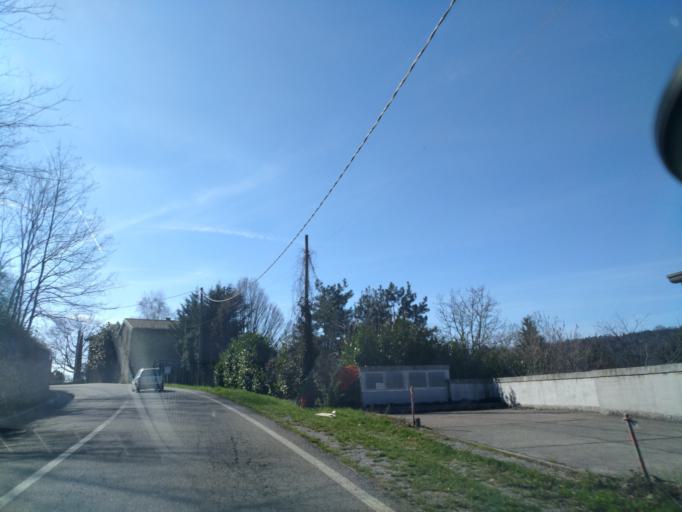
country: IT
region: Lombardy
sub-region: Provincia di Como
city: Montorfano
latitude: 45.7871
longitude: 9.1338
